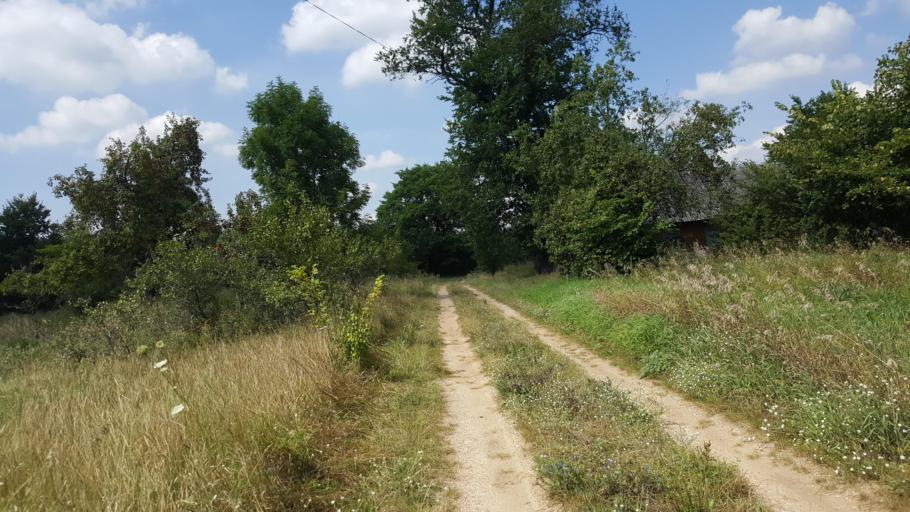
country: PL
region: Podlasie
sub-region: Powiat hajnowski
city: Hajnowka
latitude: 52.5746
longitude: 23.5490
